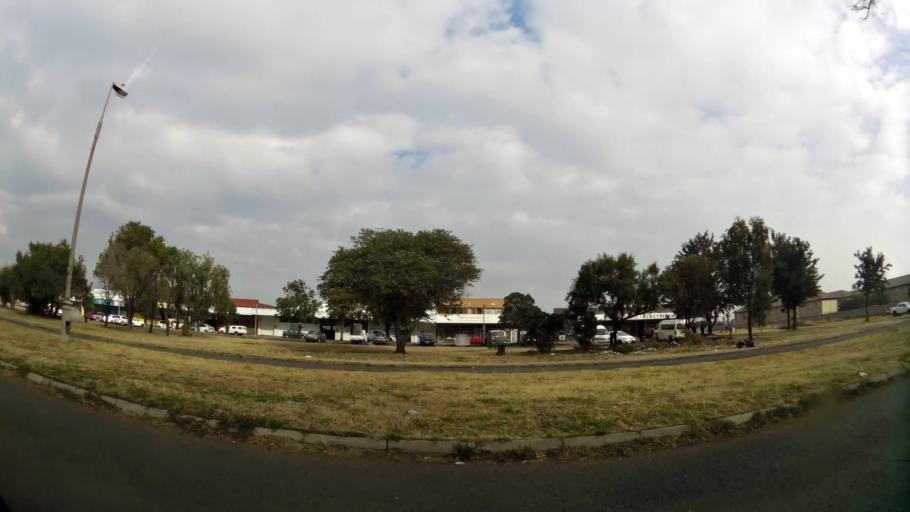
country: ZA
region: Gauteng
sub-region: Sedibeng District Municipality
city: Vanderbijlpark
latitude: -26.6959
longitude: 27.8404
